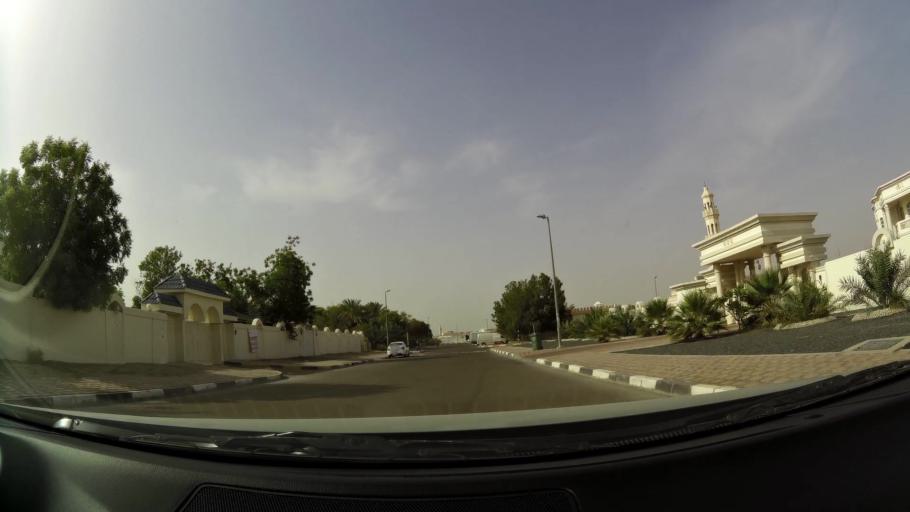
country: AE
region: Abu Dhabi
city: Al Ain
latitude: 24.1465
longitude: 55.7111
